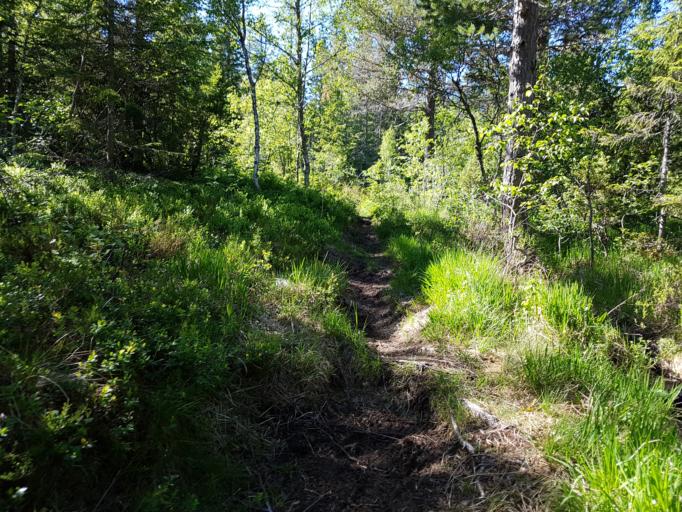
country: NO
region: Sor-Trondelag
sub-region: Trondheim
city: Trondheim
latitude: 63.4091
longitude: 10.3125
